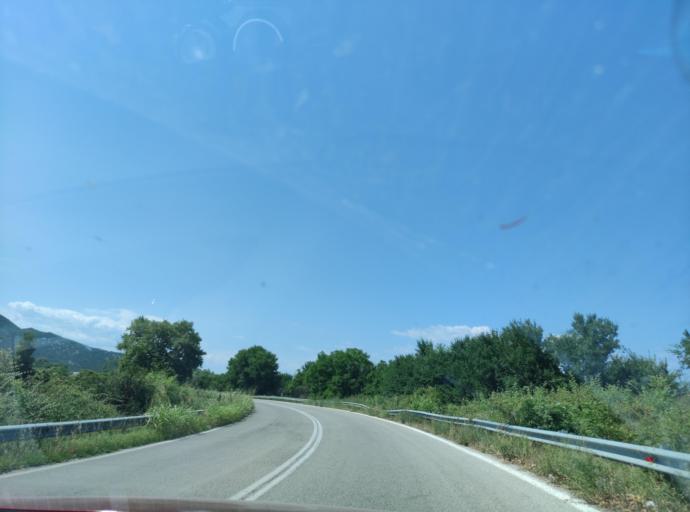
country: GR
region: East Macedonia and Thrace
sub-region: Nomos Kavalas
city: Palaiochori
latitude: 40.9565
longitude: 24.1930
